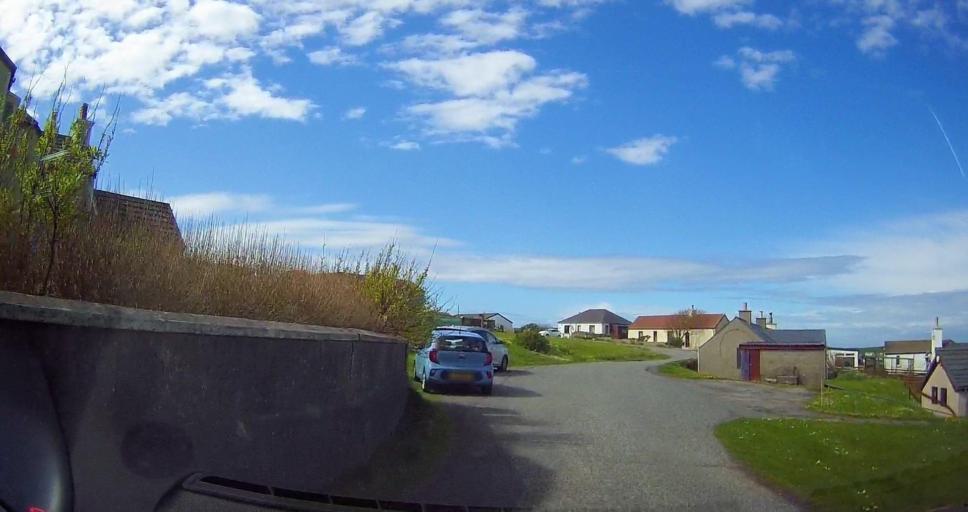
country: GB
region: Scotland
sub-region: Shetland Islands
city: Sandwick
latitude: 59.9737
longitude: -1.3236
